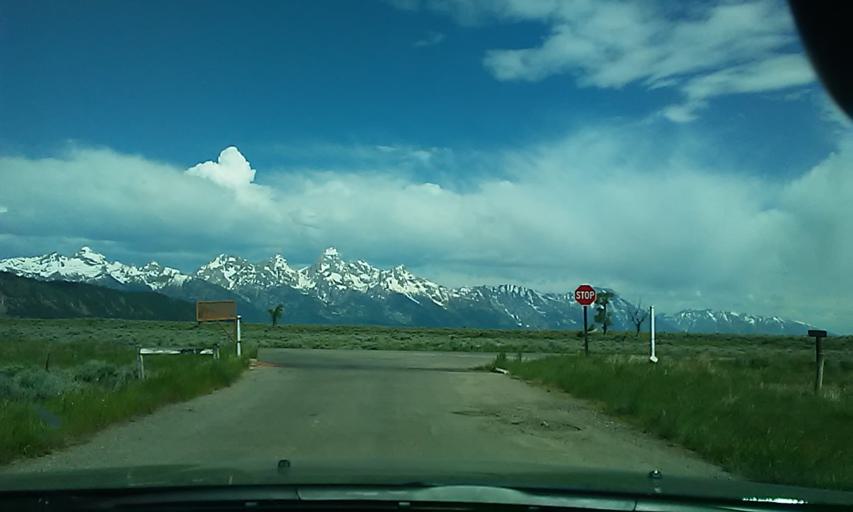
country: US
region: Wyoming
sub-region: Teton County
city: Jackson
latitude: 43.6255
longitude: -110.6241
